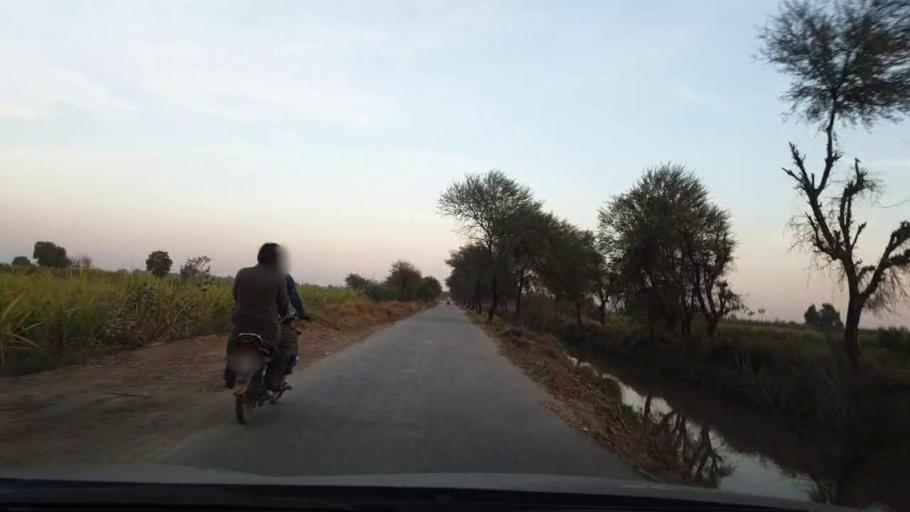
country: PK
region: Sindh
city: Tando Allahyar
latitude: 25.5920
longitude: 68.7095
